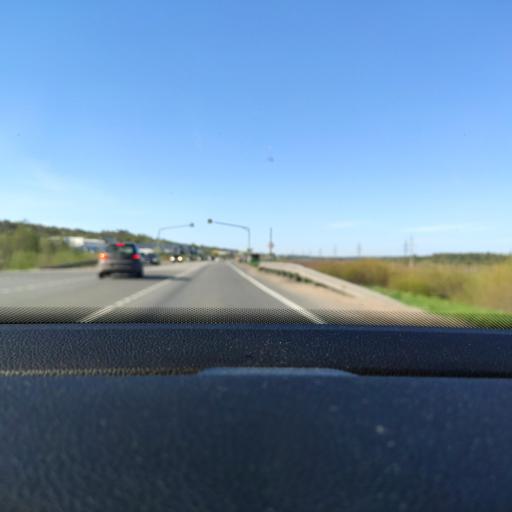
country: RU
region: Moskovskaya
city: Yakhroma
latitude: 56.3080
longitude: 37.4795
